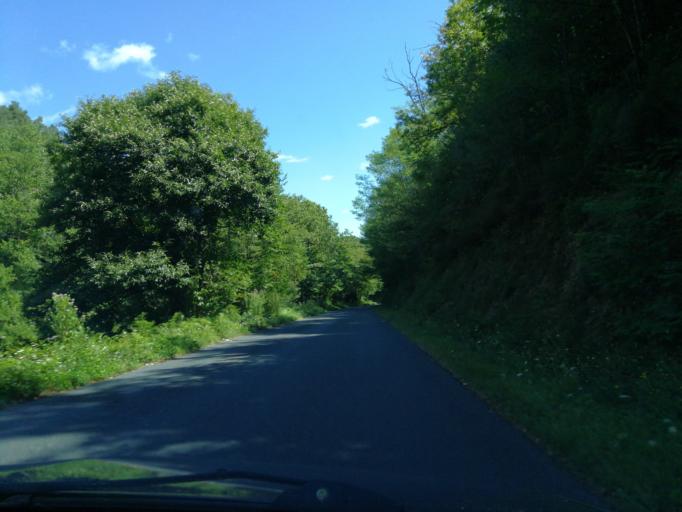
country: FR
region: Limousin
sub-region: Departement de la Correze
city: Argentat
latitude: 45.0918
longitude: 1.9136
